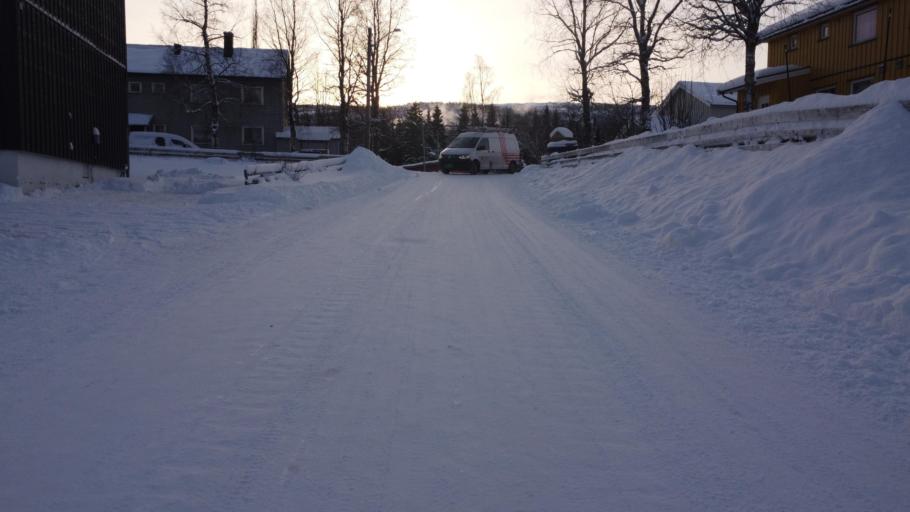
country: NO
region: Nordland
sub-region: Rana
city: Mo i Rana
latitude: 66.3158
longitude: 14.1645
